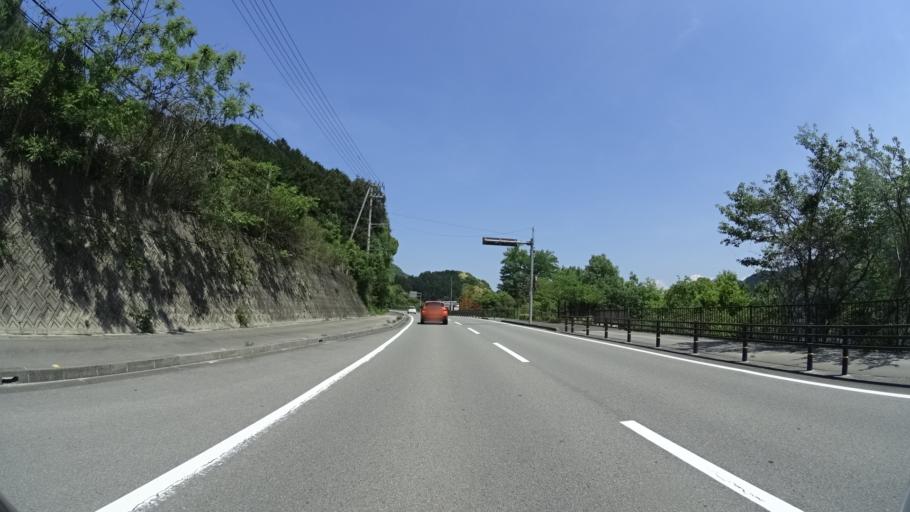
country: JP
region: Ehime
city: Hojo
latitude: 33.9940
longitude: 132.9169
